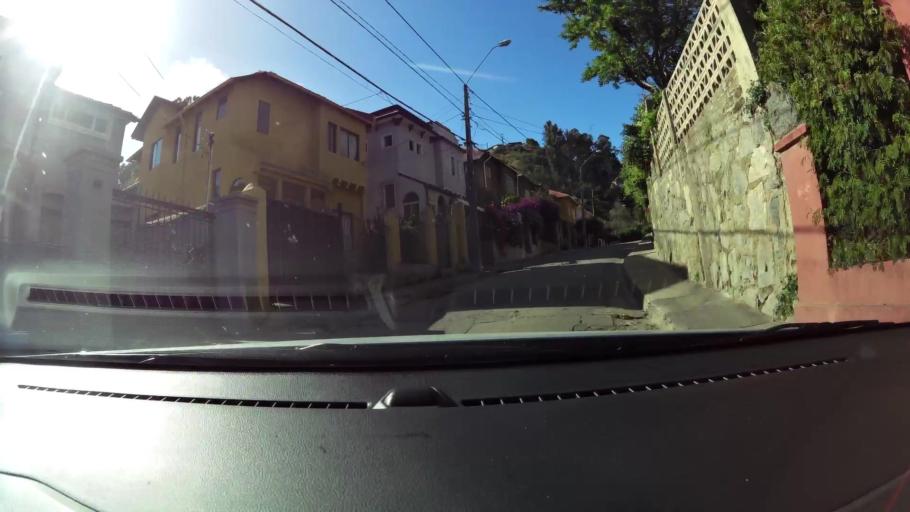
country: CL
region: Valparaiso
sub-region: Provincia de Valparaiso
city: Valparaiso
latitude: -33.0596
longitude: -71.5996
